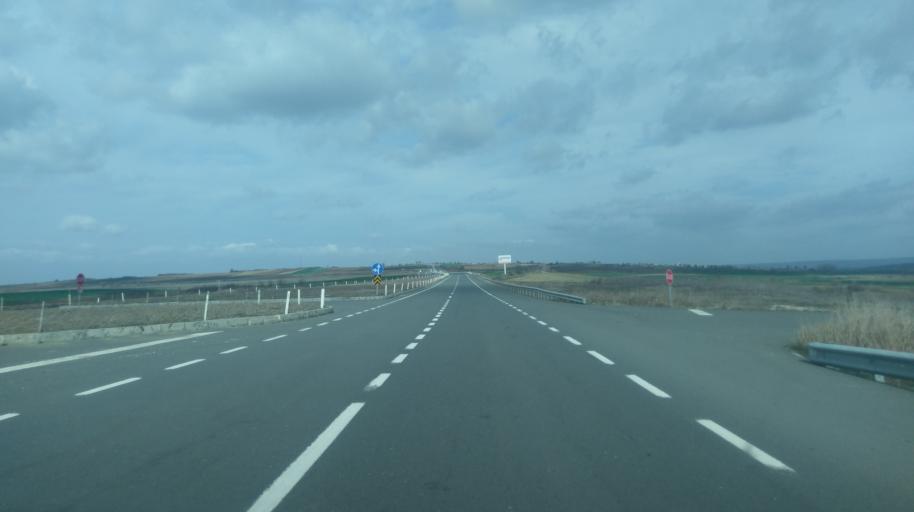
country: TR
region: Edirne
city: Hamidiye
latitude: 41.0415
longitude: 26.6344
